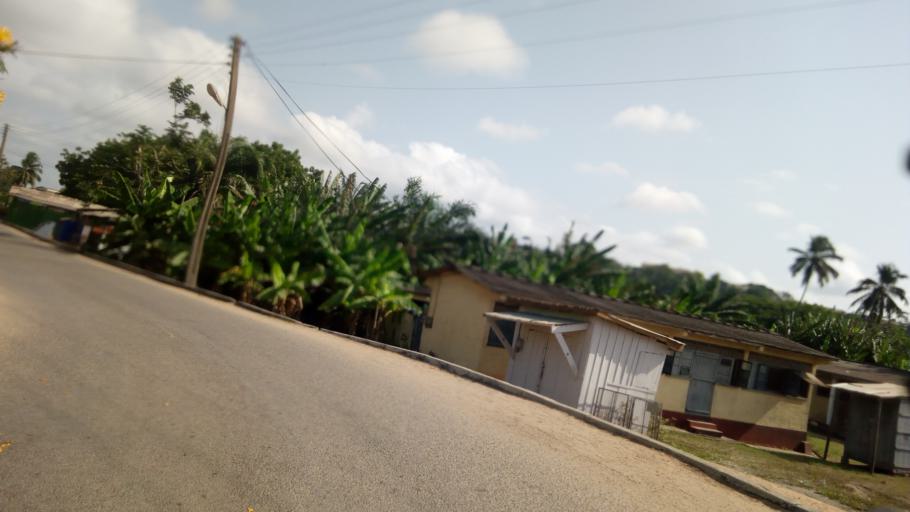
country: GH
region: Central
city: Cape Coast
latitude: 5.1170
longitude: -1.2668
